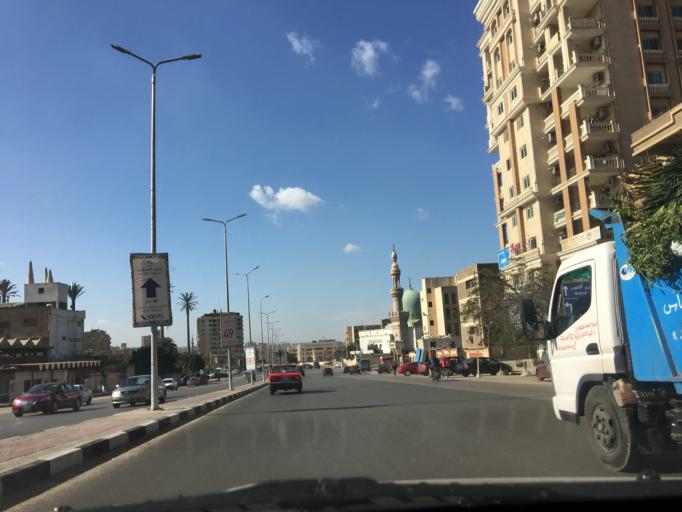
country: EG
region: Muhafazat al Qahirah
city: Cairo
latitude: 30.0528
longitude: 31.3289
